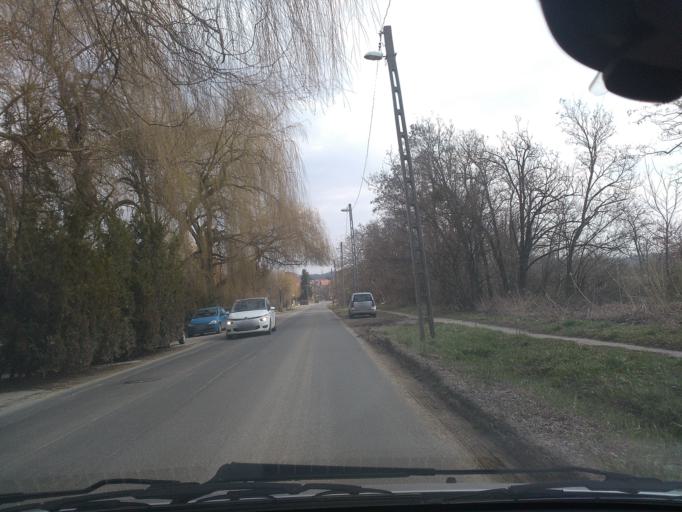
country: HU
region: Pest
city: Urom
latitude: 47.6013
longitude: 19.0046
